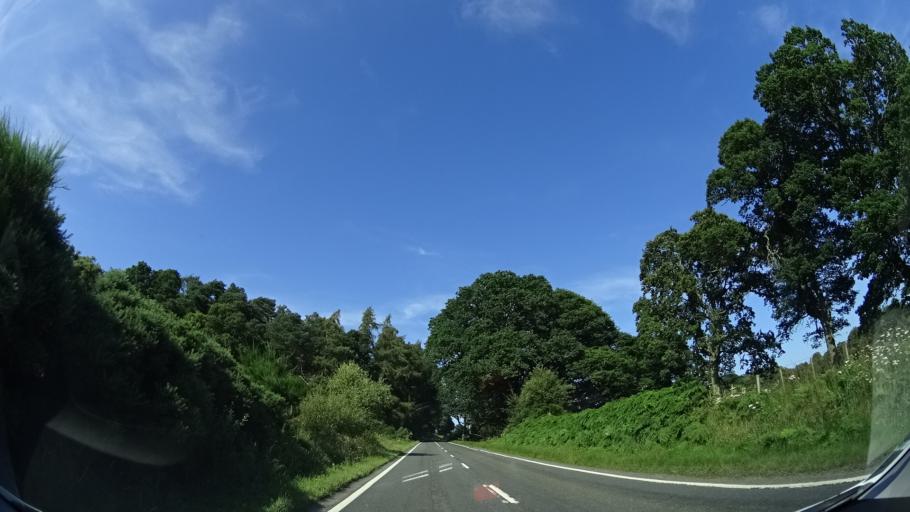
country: GB
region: Scotland
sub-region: Highland
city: Inverness
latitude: 57.4425
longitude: -4.2961
